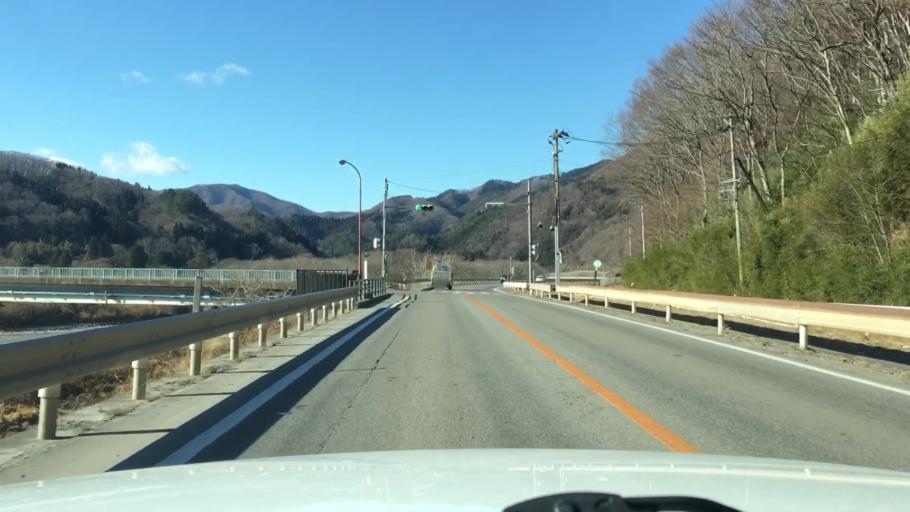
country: JP
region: Iwate
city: Miyako
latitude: 39.6297
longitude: 141.8560
